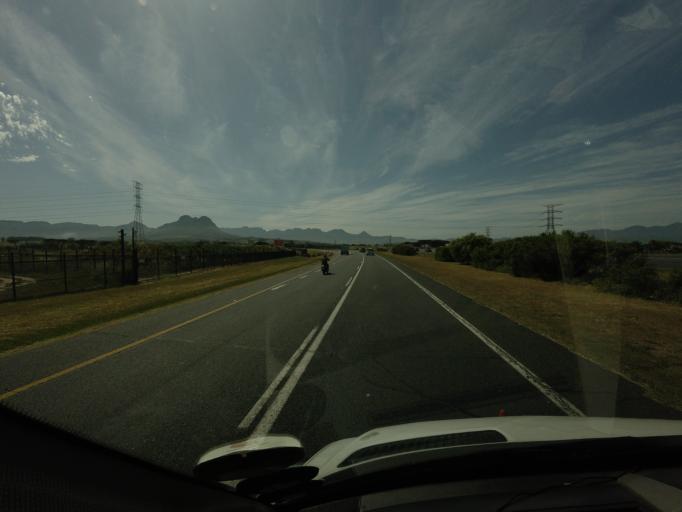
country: ZA
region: Western Cape
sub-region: Cape Winelands District Municipality
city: Stellenbosch
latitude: -34.0586
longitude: 18.7749
